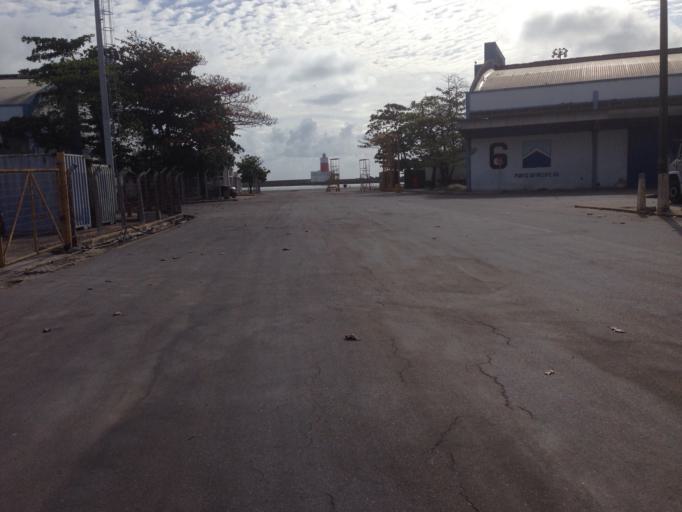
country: BR
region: Pernambuco
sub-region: Recife
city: Recife
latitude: -8.0547
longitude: -34.8690
